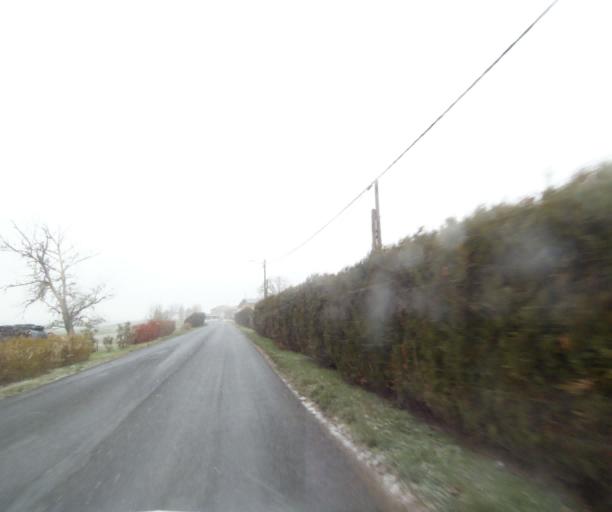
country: FR
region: Champagne-Ardenne
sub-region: Departement de la Haute-Marne
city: Wassy
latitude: 48.5132
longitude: 5.0016
